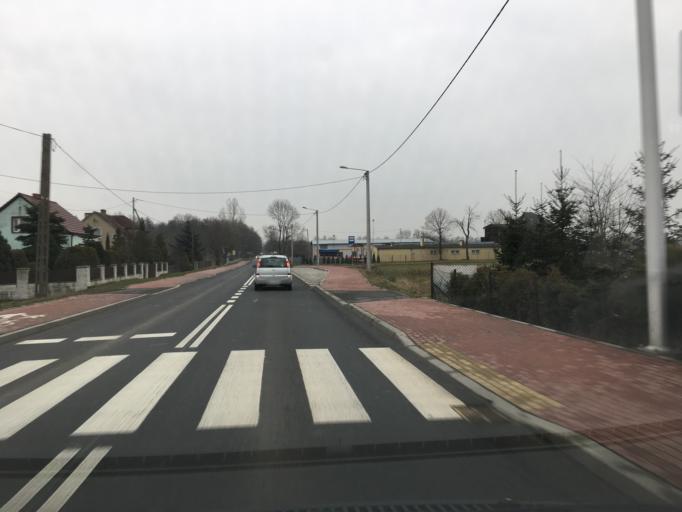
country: PL
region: Opole Voivodeship
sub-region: Powiat kedzierzynsko-kozielski
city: Bierawa
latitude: 50.3069
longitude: 18.2287
